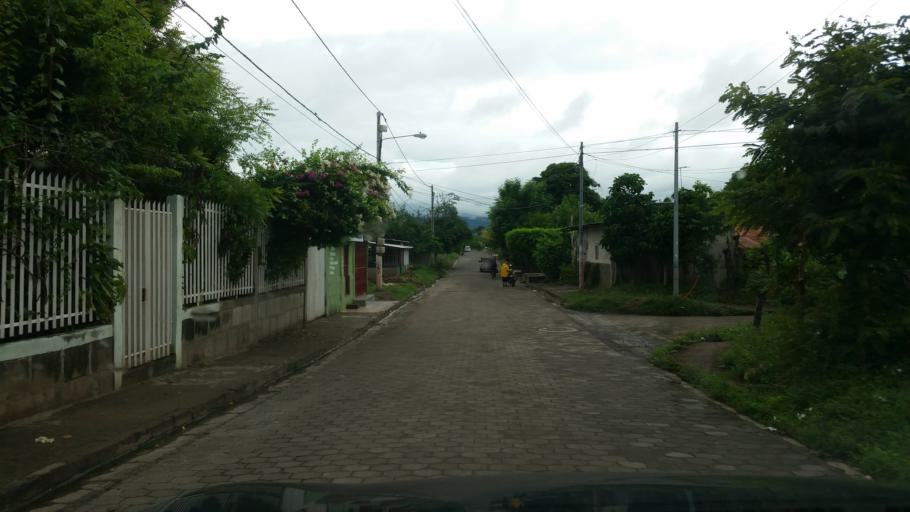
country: NI
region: Granada
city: Granada
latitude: 11.9419
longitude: -85.9544
